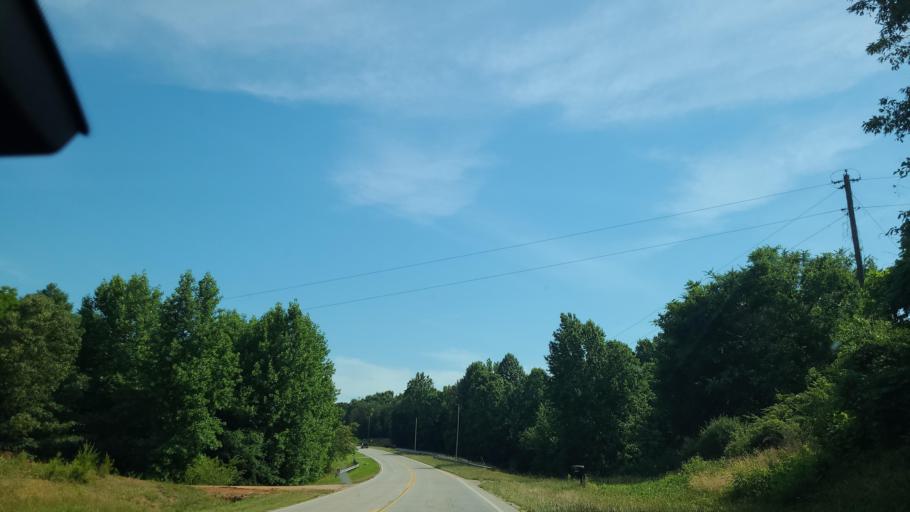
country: US
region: Georgia
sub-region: Franklin County
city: Gumlog
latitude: 34.5657
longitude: -83.0488
